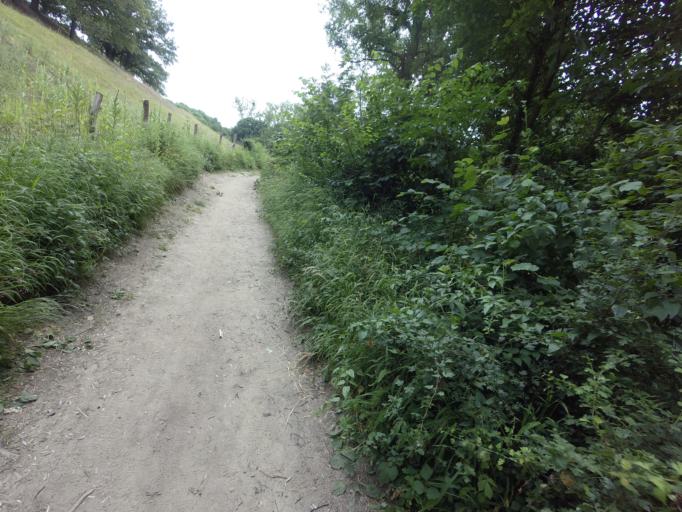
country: NL
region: Limburg
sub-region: Valkenburg aan de Geul
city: Berg
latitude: 50.8501
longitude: 5.7729
